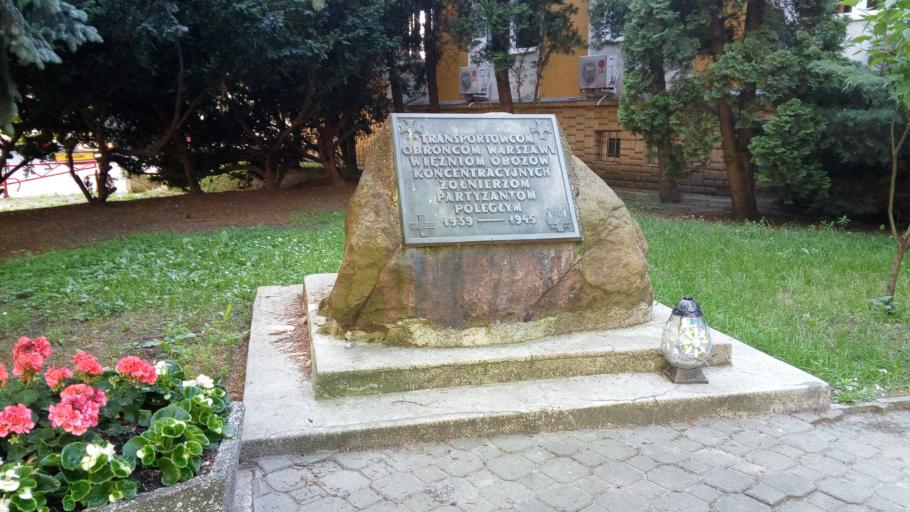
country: PL
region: Masovian Voivodeship
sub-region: Warszawa
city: Ochota
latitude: 52.2125
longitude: 20.9701
